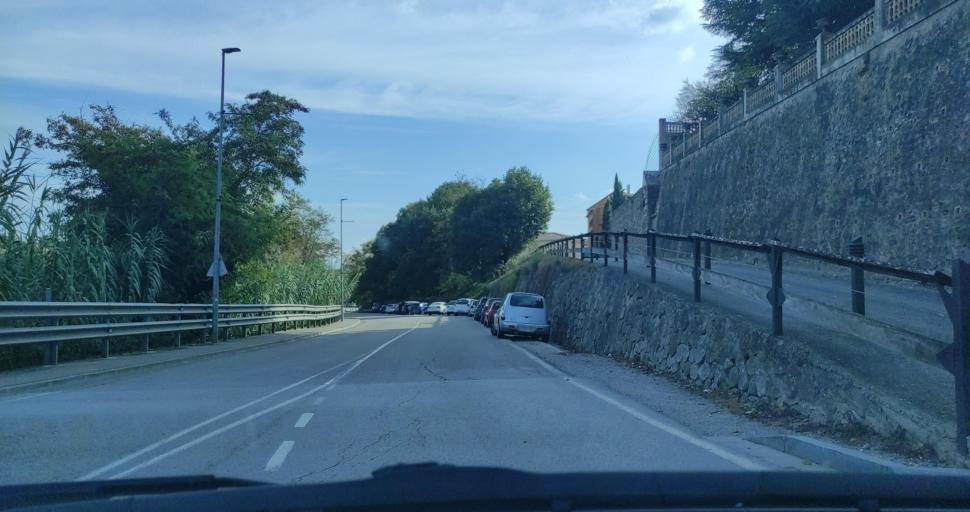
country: ES
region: Catalonia
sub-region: Provincia de Girona
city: Besalu
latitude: 42.2004
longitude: 2.6991
